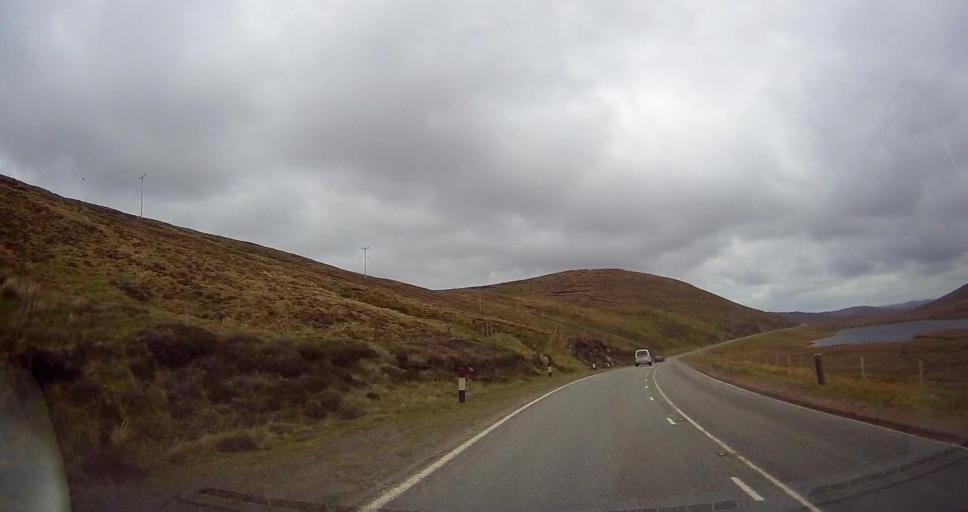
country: GB
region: Scotland
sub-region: Shetland Islands
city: Lerwick
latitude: 60.3212
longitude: -1.2502
